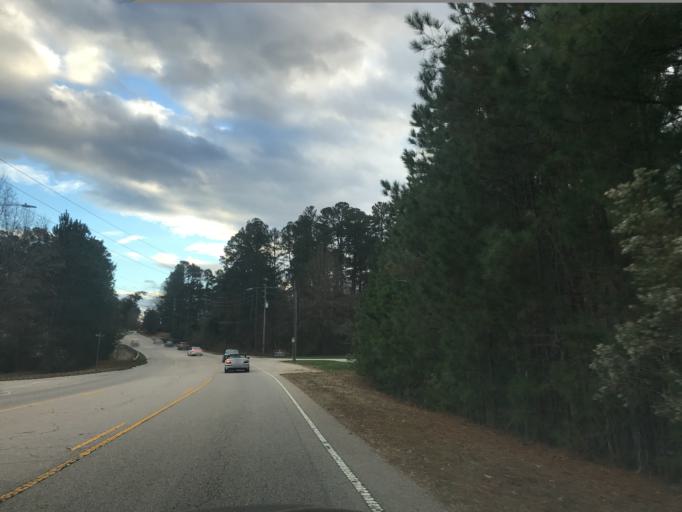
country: US
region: North Carolina
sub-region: Wake County
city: West Raleigh
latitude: 35.8533
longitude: -78.6726
